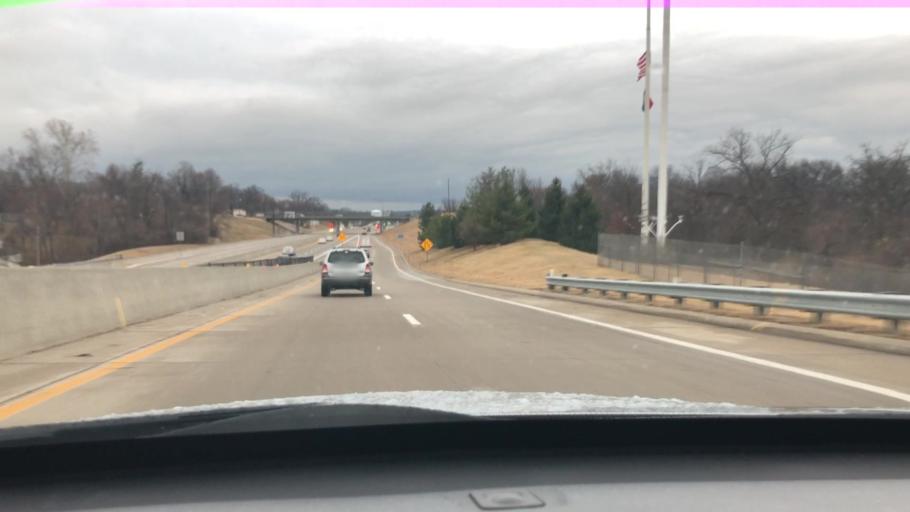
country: US
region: Missouri
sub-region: Saint Louis County
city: Valley Park
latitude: 38.5668
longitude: -90.5001
